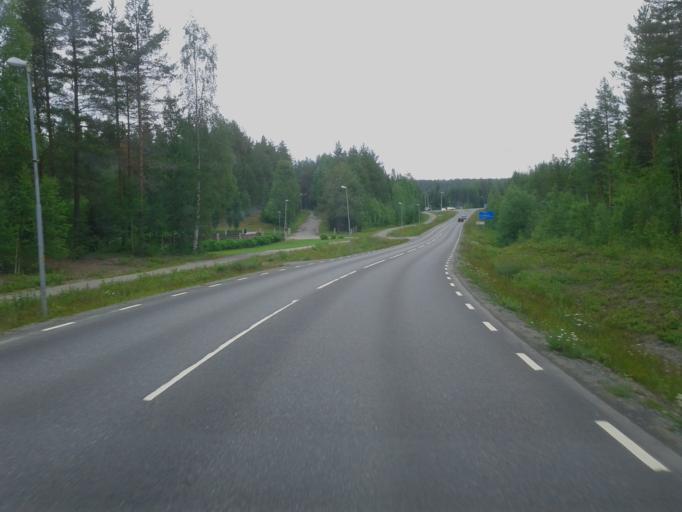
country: SE
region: Vaesterbotten
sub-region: Skelleftea Kommun
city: Boliden
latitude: 64.8756
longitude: 20.3883
